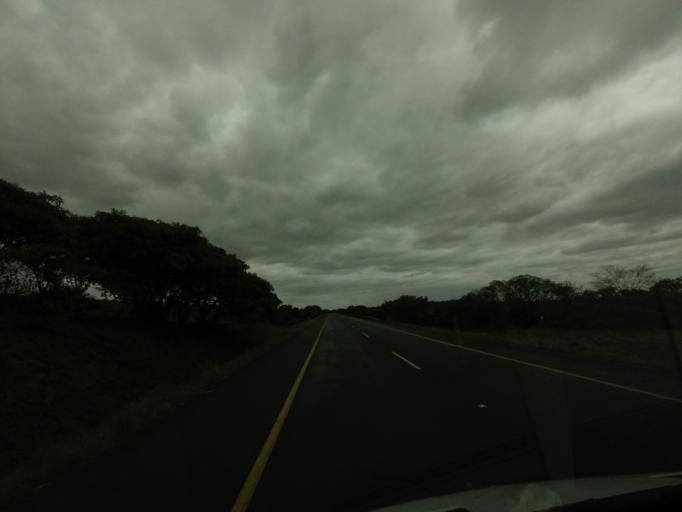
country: ZA
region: KwaZulu-Natal
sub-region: uMkhanyakude District Municipality
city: Hluhluwe
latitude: -27.9134
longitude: 32.2059
